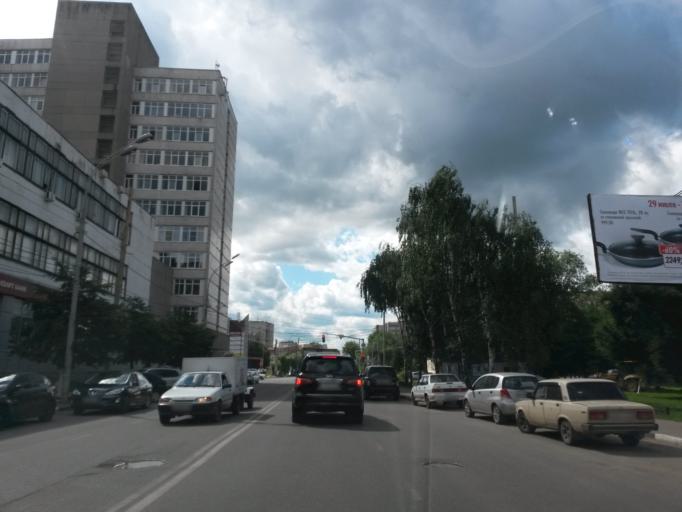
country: RU
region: Jaroslavl
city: Yaroslavl
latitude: 57.6279
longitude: 39.8486
